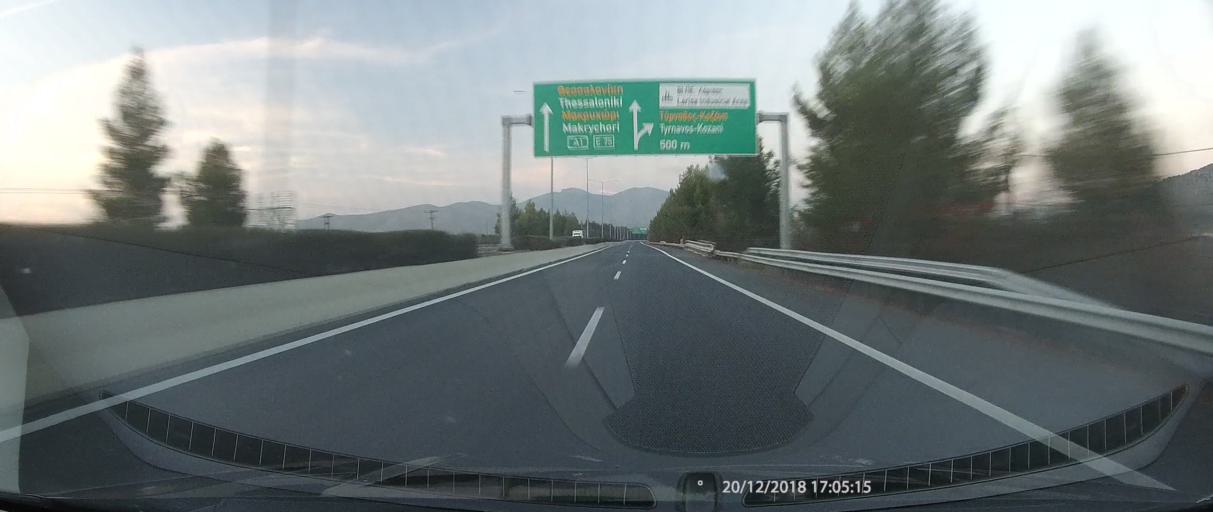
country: GR
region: Thessaly
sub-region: Nomos Larisis
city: Makrychori
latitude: 39.7355
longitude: 22.4775
